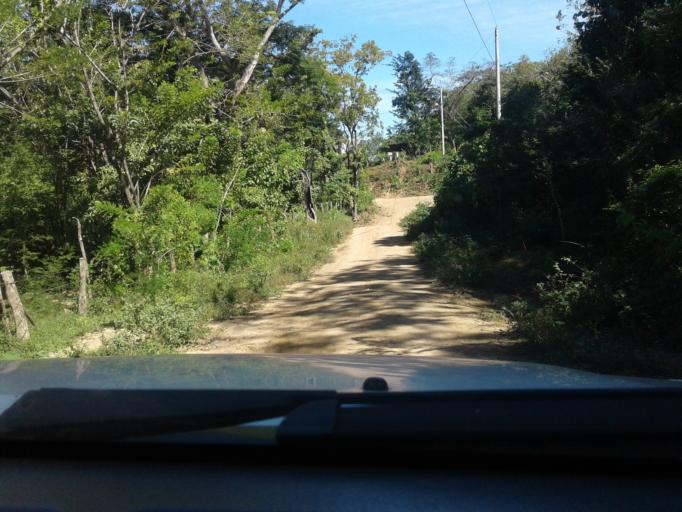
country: NI
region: Carazo
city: Santa Teresa
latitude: 11.6704
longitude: -86.1741
